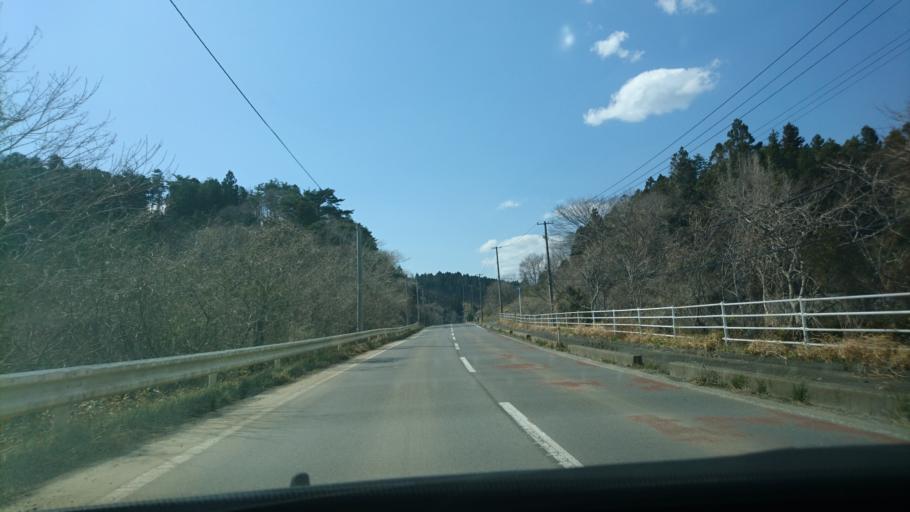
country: JP
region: Miyagi
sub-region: Oshika Gun
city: Onagawa Cho
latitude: 38.6363
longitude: 141.5051
